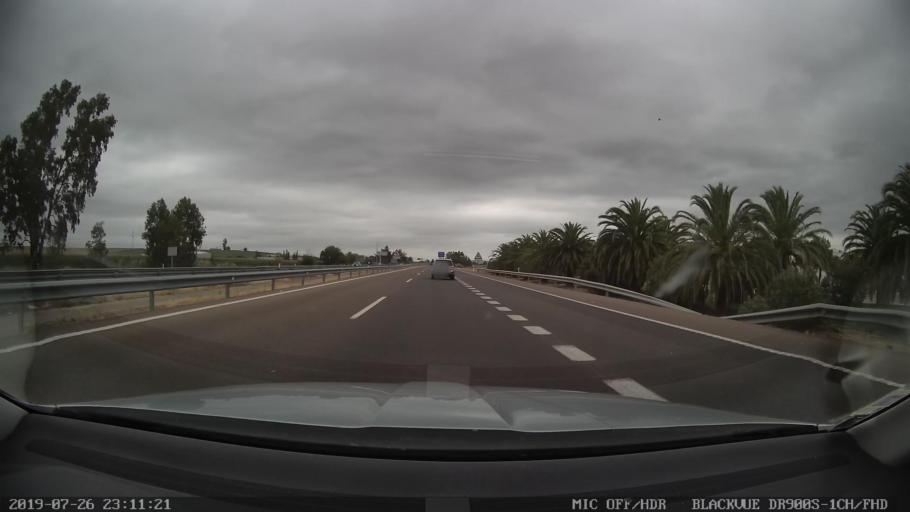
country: ES
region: Extremadura
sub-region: Provincia de Badajoz
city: San Pedro de Merida
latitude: 38.9906
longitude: -6.1110
